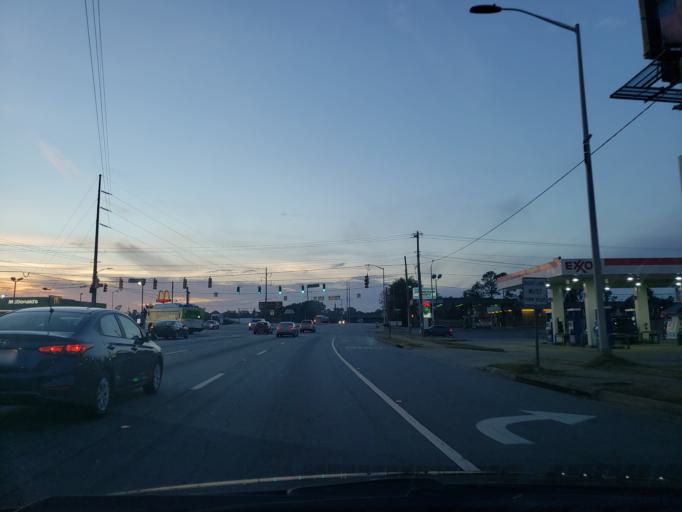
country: US
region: Georgia
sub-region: Dougherty County
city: Albany
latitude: 31.5710
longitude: -84.1069
